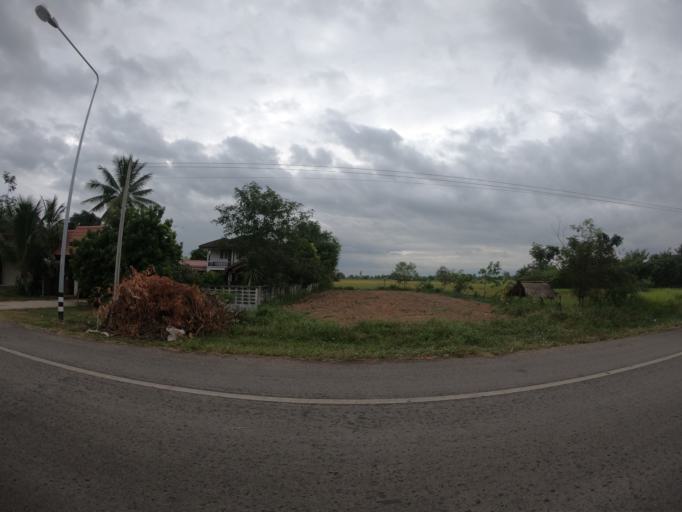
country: TH
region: Roi Et
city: Chiang Khwan
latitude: 16.1299
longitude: 103.8497
